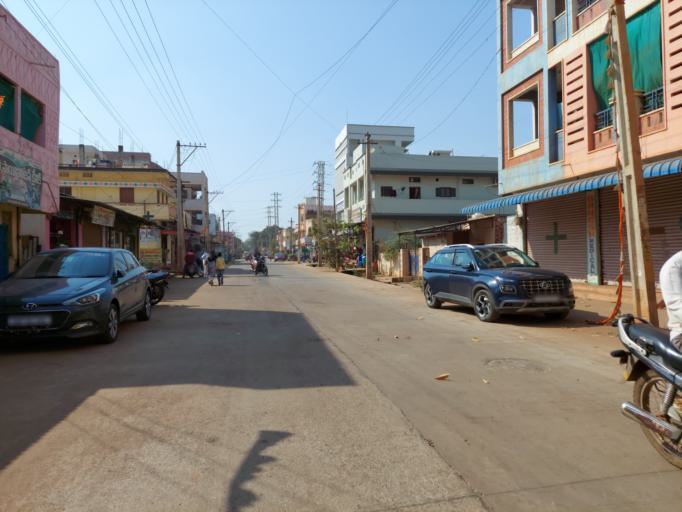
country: IN
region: Telangana
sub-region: Rangareddi
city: Vikarabad
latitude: 17.3372
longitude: 77.9032
